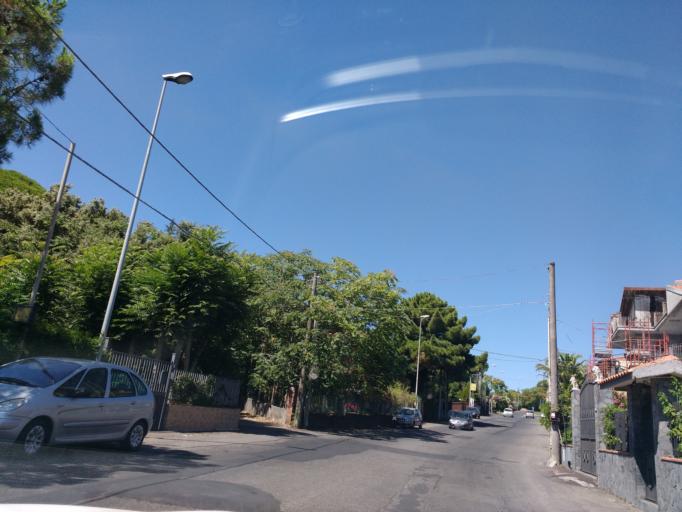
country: IT
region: Sicily
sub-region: Catania
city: Nicolosi
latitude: 37.6089
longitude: 15.0206
